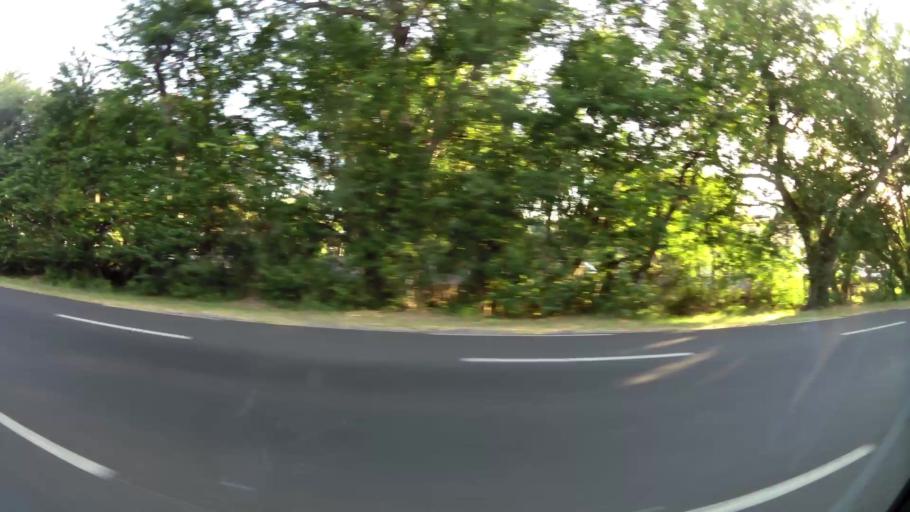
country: RE
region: Reunion
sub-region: Reunion
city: Trois-Bassins
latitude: -21.0881
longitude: 55.2336
